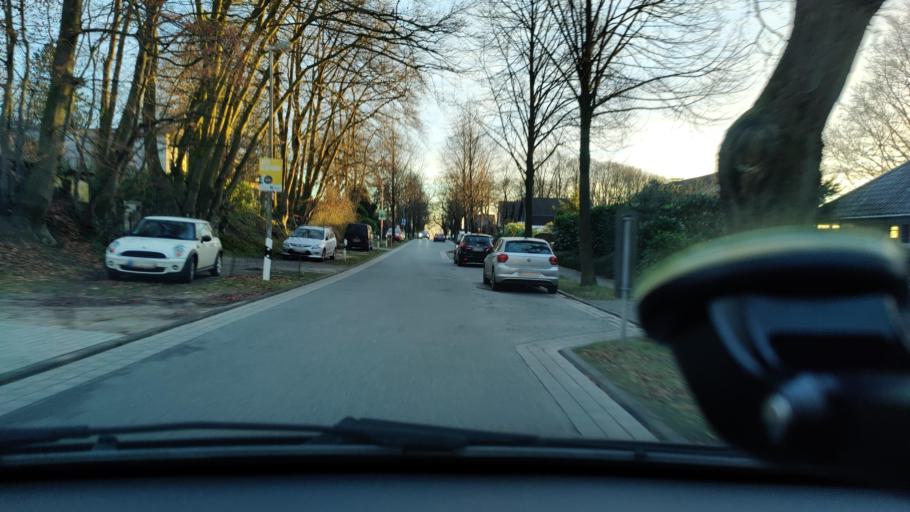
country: DE
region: North Rhine-Westphalia
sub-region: Regierungsbezirk Dusseldorf
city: Kleve
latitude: 51.7856
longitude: 6.1090
